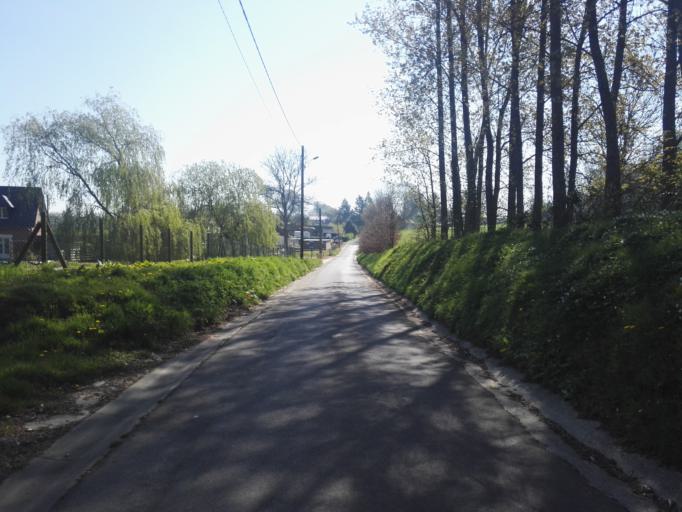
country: FR
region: Haute-Normandie
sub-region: Departement de la Seine-Maritime
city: Doudeville
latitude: 49.7502
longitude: 0.7315
